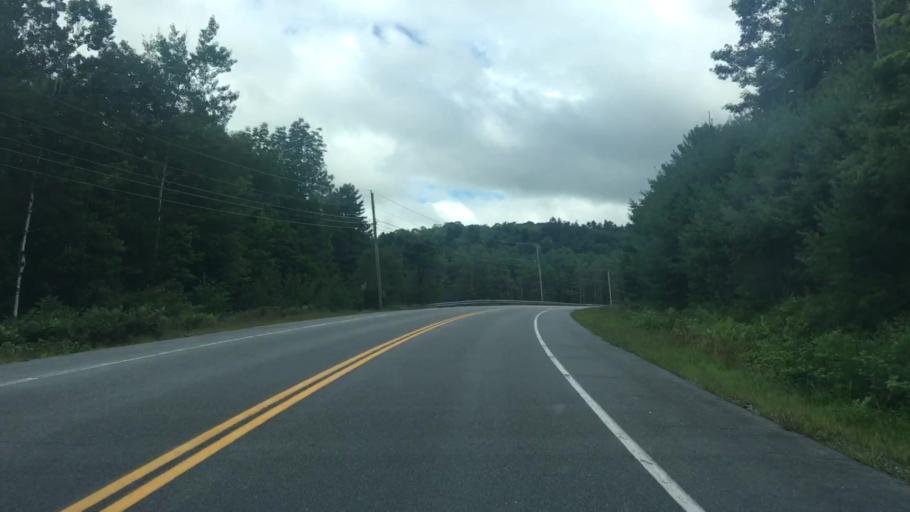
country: US
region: Maine
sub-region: York County
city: Cornish
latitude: 43.7547
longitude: -70.8132
